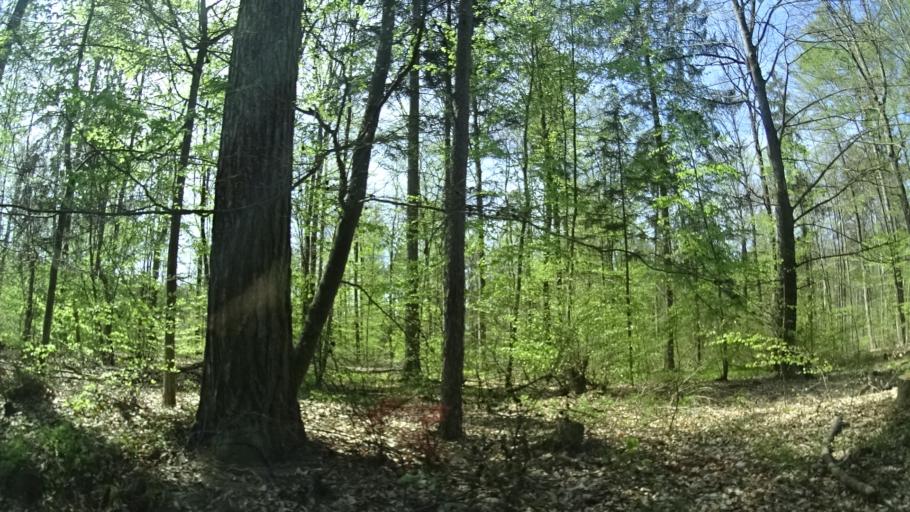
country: DE
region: Thuringia
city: Hellingen
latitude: 50.2823
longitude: 10.7640
